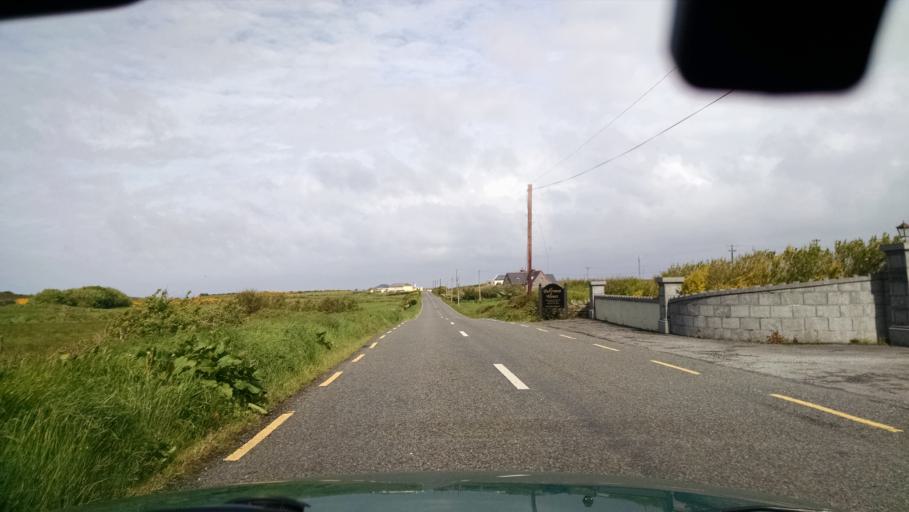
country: IE
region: Connaught
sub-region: County Galway
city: Bearna
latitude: 53.0112
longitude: -9.3656
